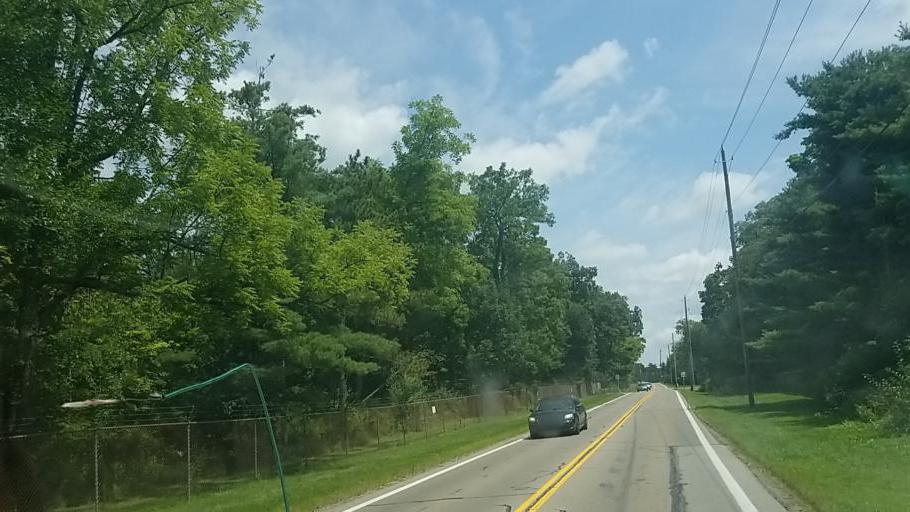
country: US
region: Ohio
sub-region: Franklin County
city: Reynoldsburg
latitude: 39.9299
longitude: -82.7786
